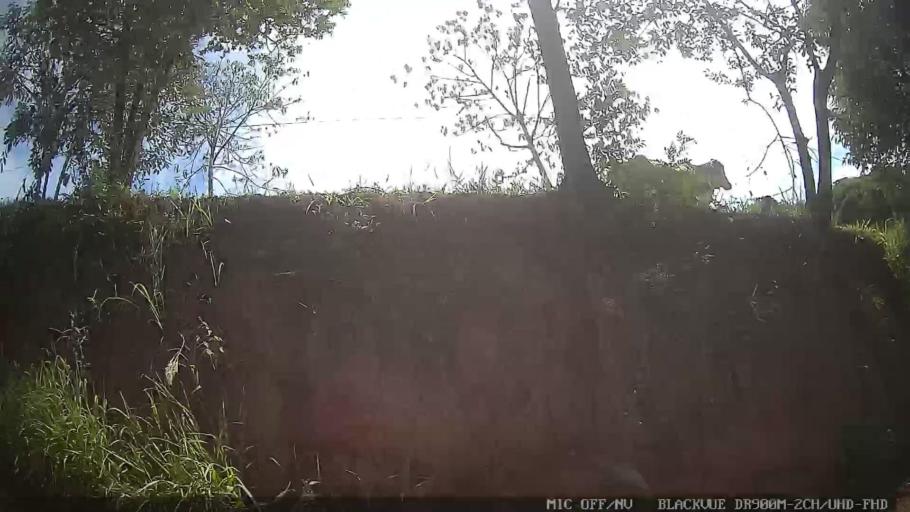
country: BR
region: Sao Paulo
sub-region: Braganca Paulista
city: Braganca Paulista
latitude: -23.0216
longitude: -46.6390
